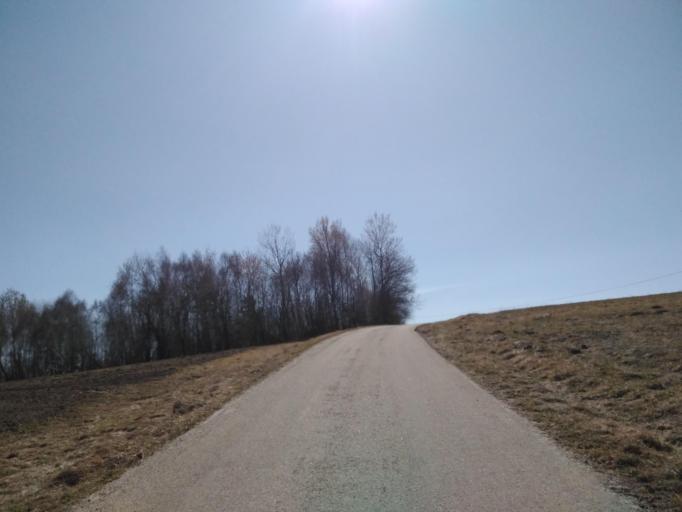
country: PL
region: Subcarpathian Voivodeship
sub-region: Powiat brzozowski
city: Jablonica Polska
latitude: 49.7451
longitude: 21.8938
